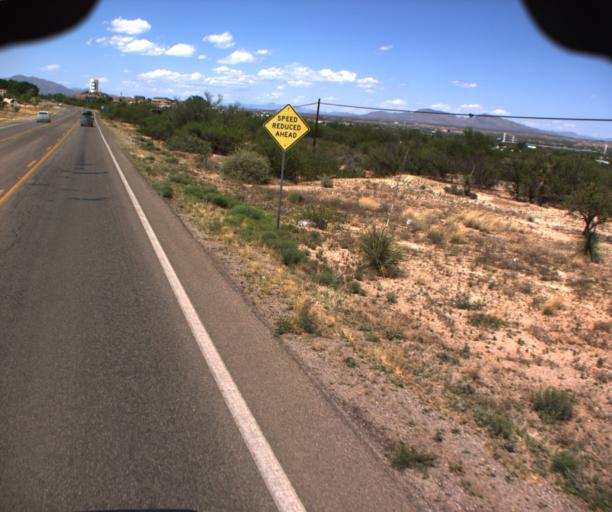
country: US
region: Arizona
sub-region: Cochise County
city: Benson
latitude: 31.9601
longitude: -110.2877
